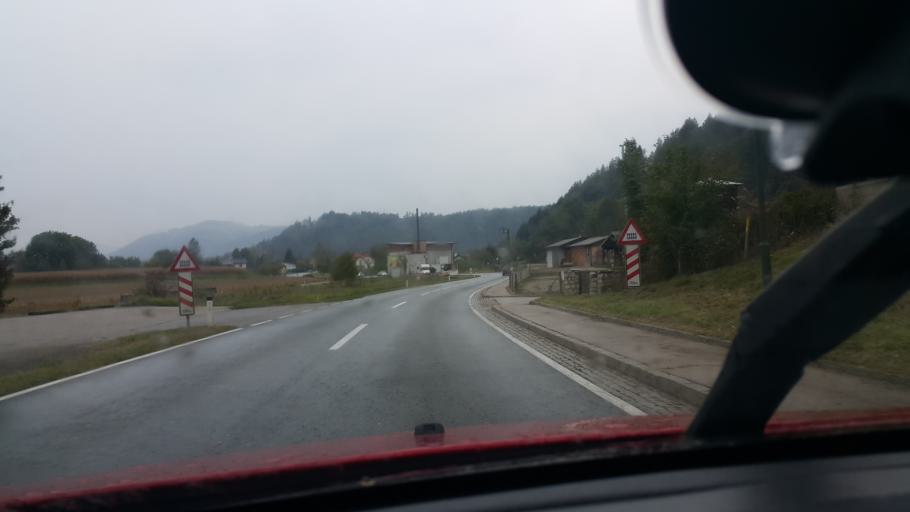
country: AT
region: Carinthia
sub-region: Politischer Bezirk Wolfsberg
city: Lavamund
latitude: 46.6381
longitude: 14.9532
